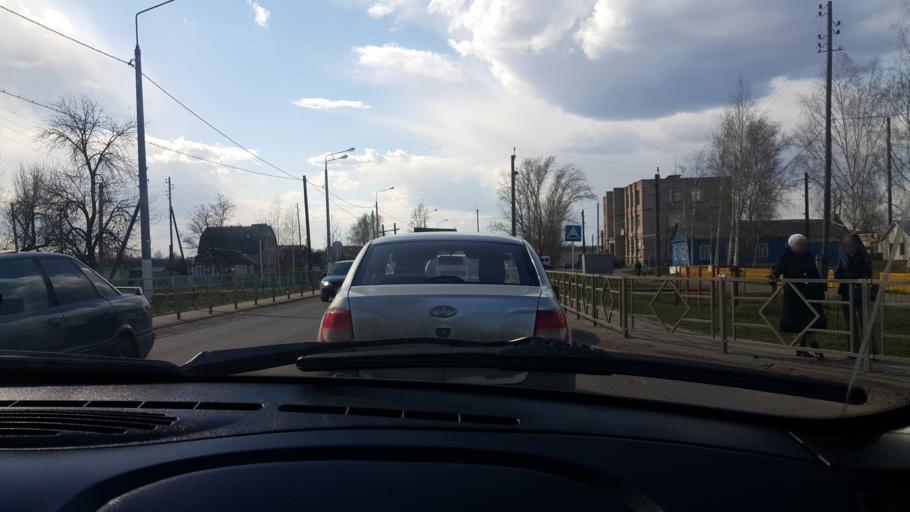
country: RU
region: Tambov
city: Zavoronezhskoye
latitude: 52.8812
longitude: 40.5477
